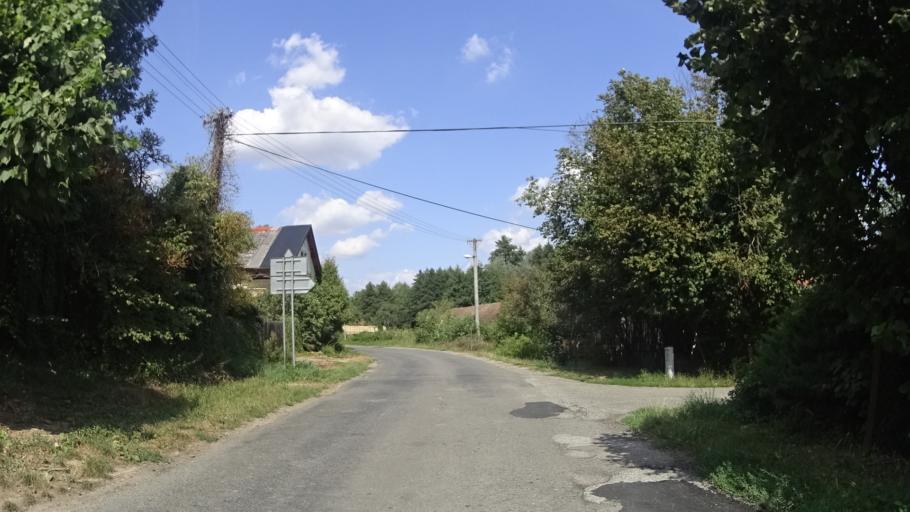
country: CZ
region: Kralovehradecky
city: Kopidlno
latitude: 50.3773
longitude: 15.3146
